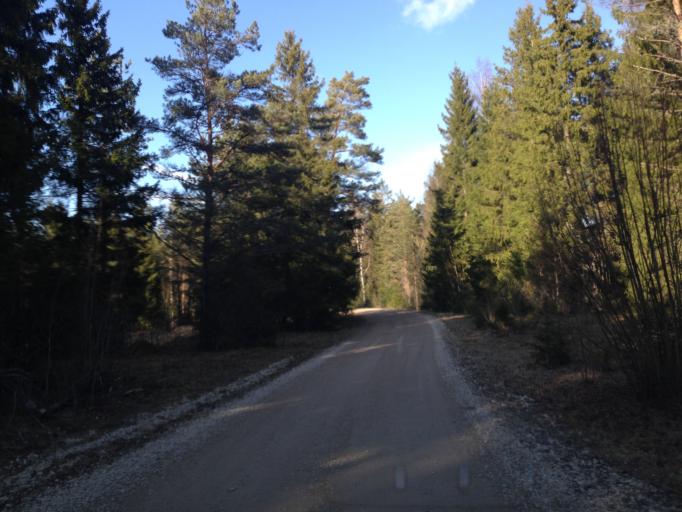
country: EE
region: Harju
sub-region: Nissi vald
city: Turba
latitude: 59.1029
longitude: 24.1546
